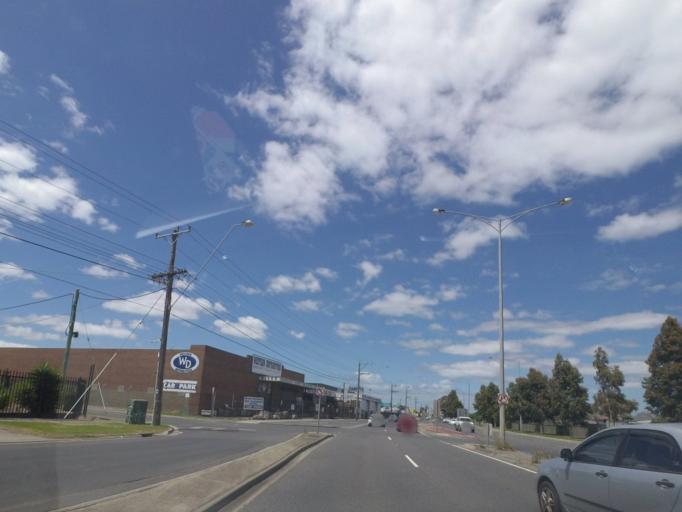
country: AU
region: Victoria
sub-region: Brimbank
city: Albion
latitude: -37.7525
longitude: 144.8331
